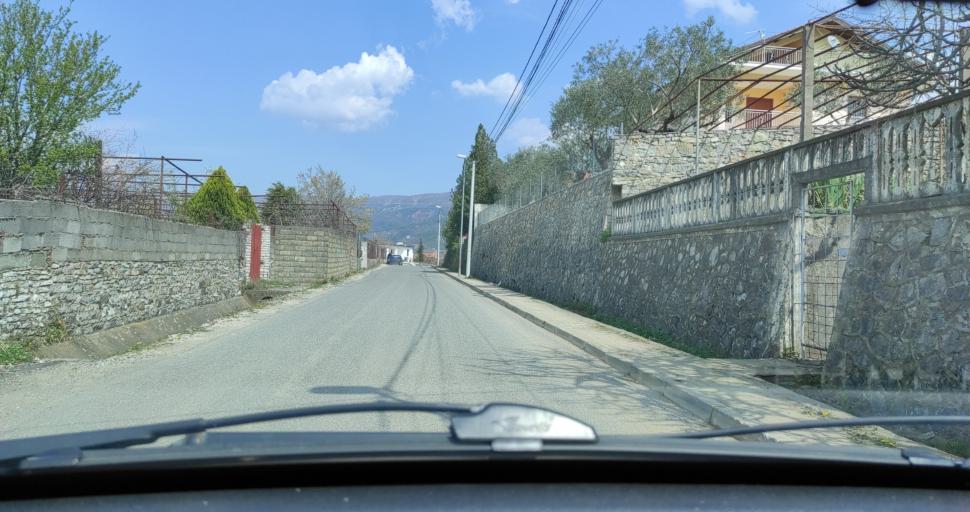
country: AL
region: Lezhe
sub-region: Rrethi i Lezhes
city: Kallmeti i Madh
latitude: 41.8500
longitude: 19.6912
